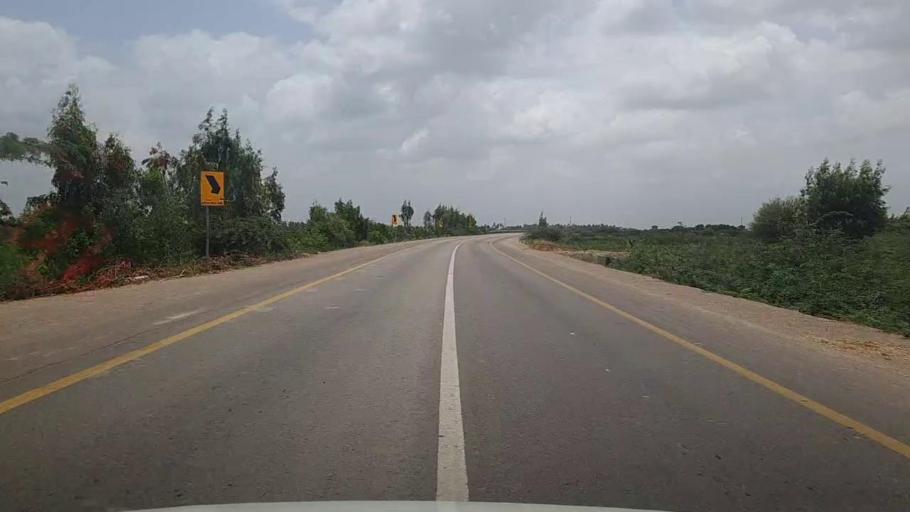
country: PK
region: Sindh
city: Thatta
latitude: 24.7390
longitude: 67.9467
